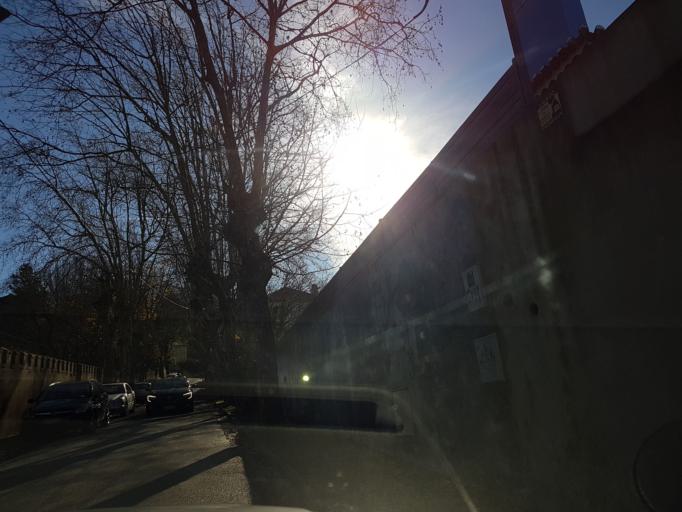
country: PT
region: Lisbon
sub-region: Sintra
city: Sintra
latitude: 38.7972
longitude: -9.3815
